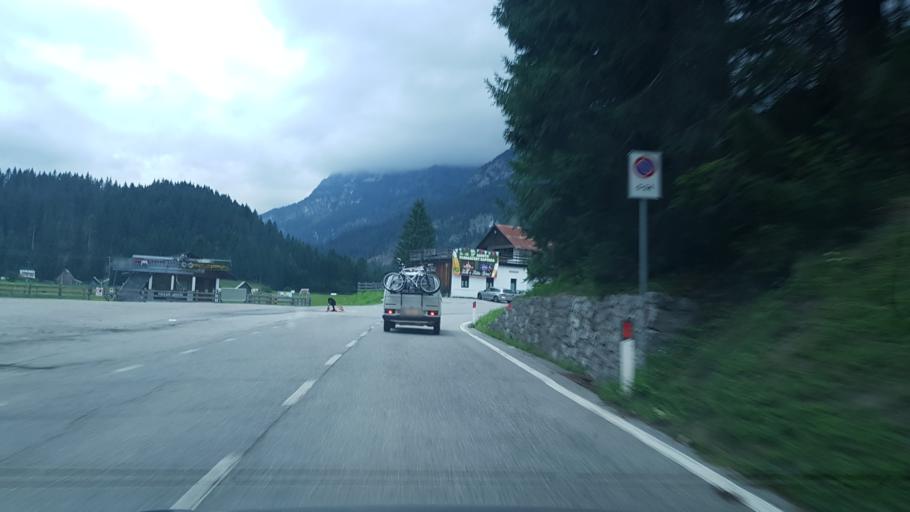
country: IT
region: Veneto
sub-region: Provincia di Belluno
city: Granvilla
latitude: 46.5662
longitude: 12.7203
